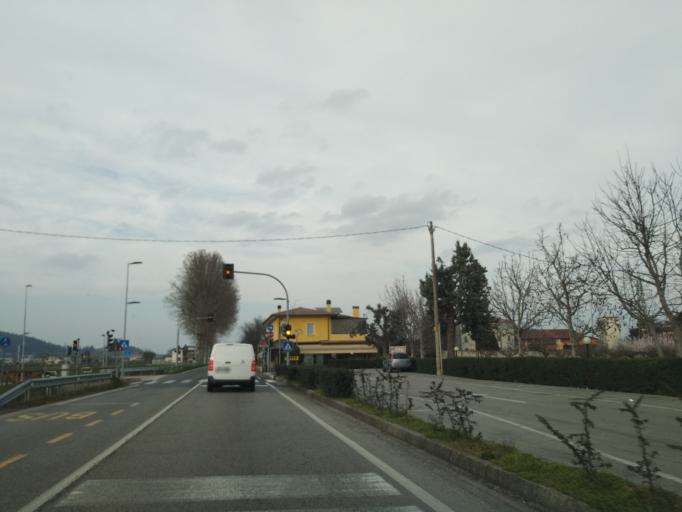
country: IT
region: Veneto
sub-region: Provincia di Vicenza
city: Lumignano
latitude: 45.4535
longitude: 11.6024
